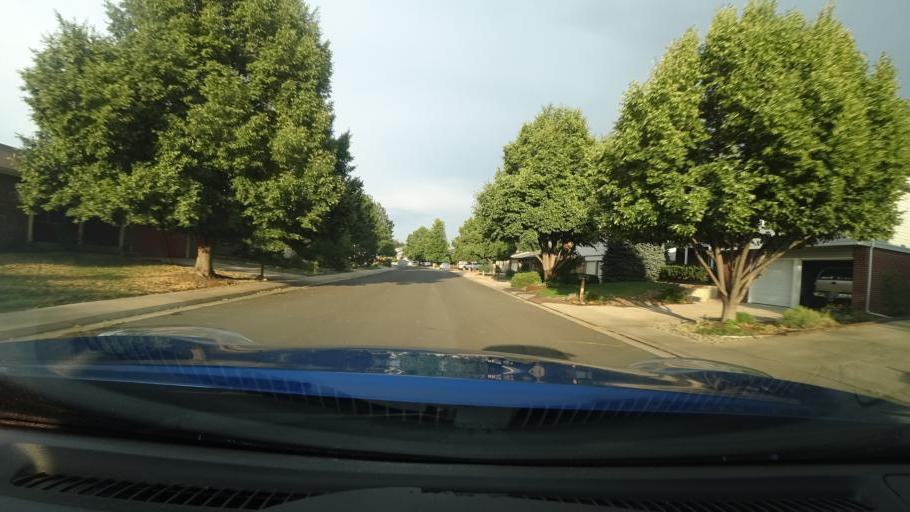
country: US
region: Colorado
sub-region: Adams County
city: Aurora
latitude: 39.6898
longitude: -104.8243
